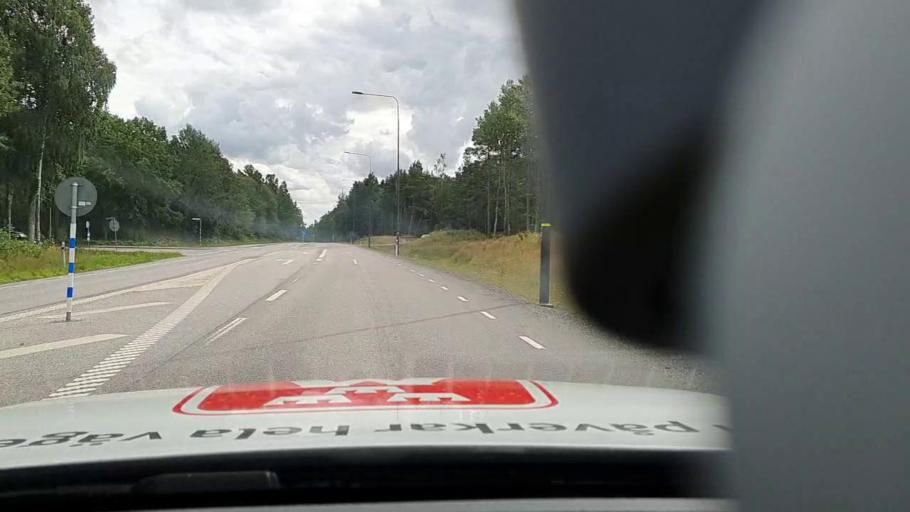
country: SE
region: Vaestra Goetaland
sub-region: Lidkopings Kommun
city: Lidkoping
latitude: 58.5343
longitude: 13.1101
